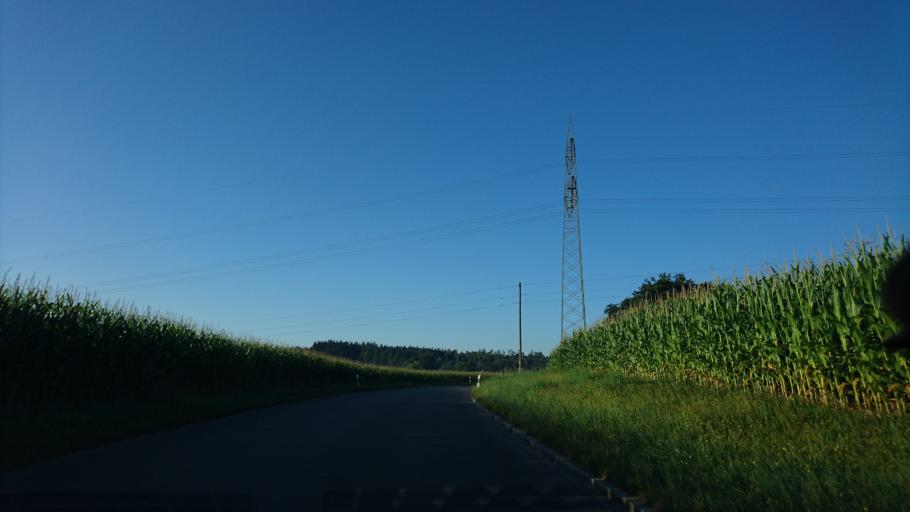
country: DE
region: Bavaria
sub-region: Swabia
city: Grossaitingen
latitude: 48.2544
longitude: 10.7371
